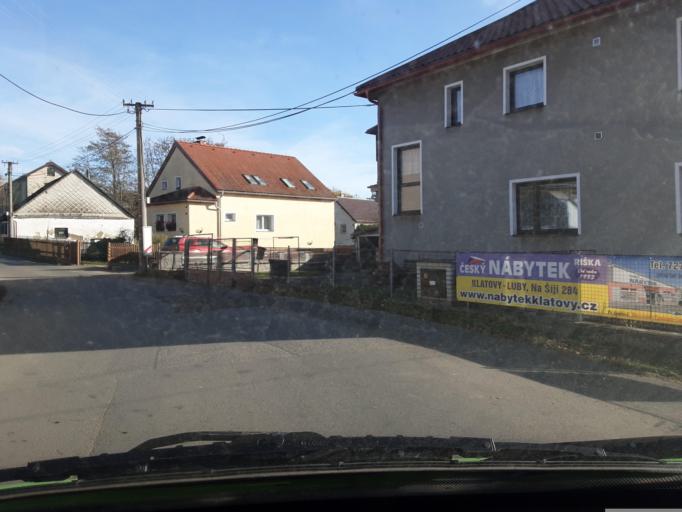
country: CZ
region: Plzensky
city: Klatovy
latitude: 49.3746
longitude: 13.3034
